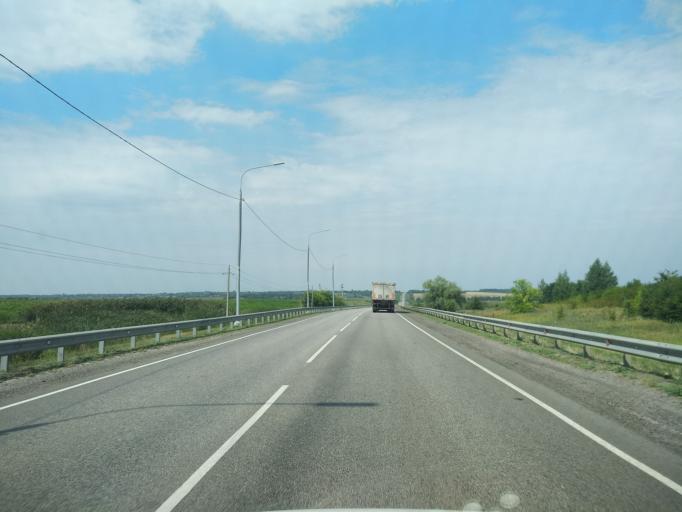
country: RU
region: Voronezj
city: Orlovo
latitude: 51.6754
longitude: 39.7605
